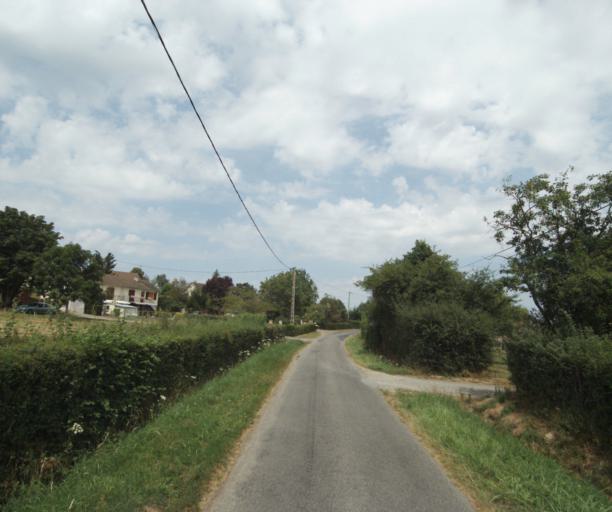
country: FR
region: Bourgogne
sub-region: Departement de Saone-et-Loire
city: Gueugnon
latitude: 46.5888
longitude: 4.0405
